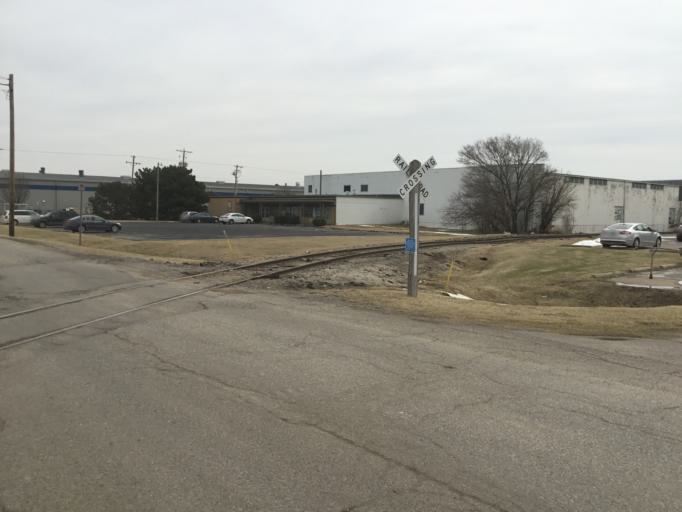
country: US
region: Kansas
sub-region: Sedgwick County
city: Wichita
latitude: 37.7449
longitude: -97.3311
